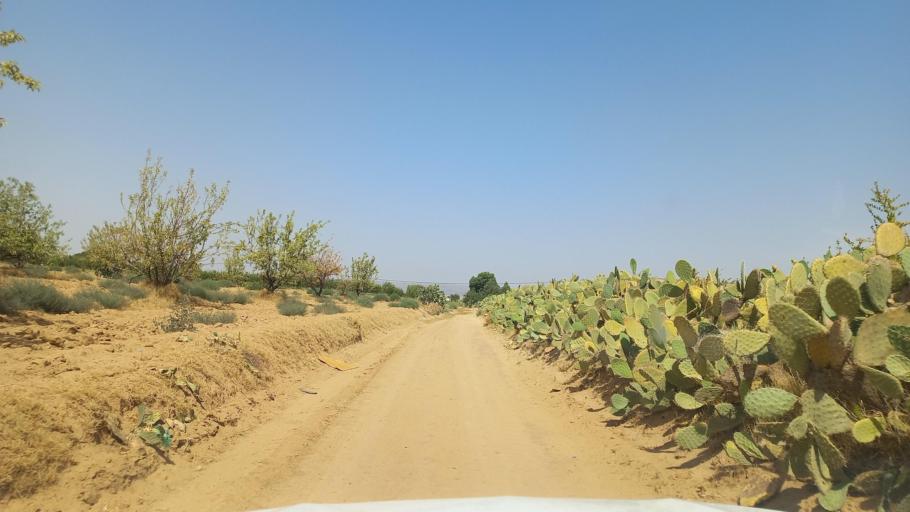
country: TN
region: Al Qasrayn
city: Kasserine
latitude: 35.2443
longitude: 9.0444
